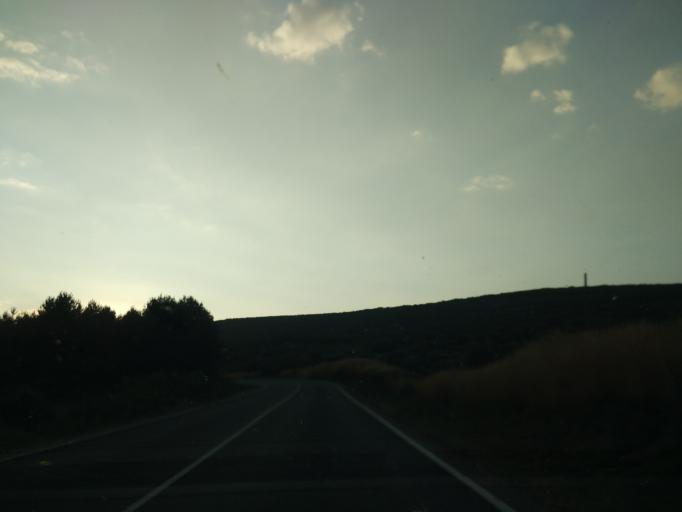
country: ES
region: Castille and Leon
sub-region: Provincia de Avila
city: San Martin del Pimpollar
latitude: 40.3736
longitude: -5.0214
